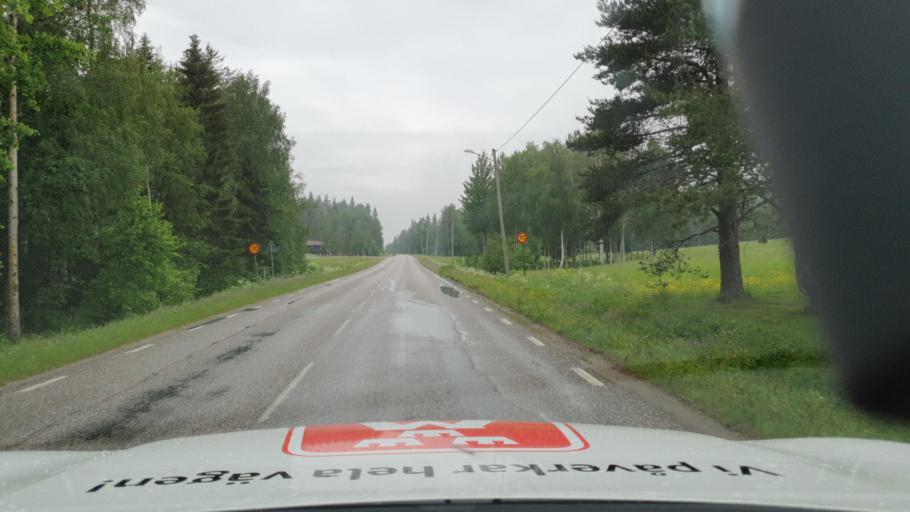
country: SE
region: Vaesterbotten
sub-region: Vannas Kommun
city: Vaennaes
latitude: 63.7708
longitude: 19.6177
